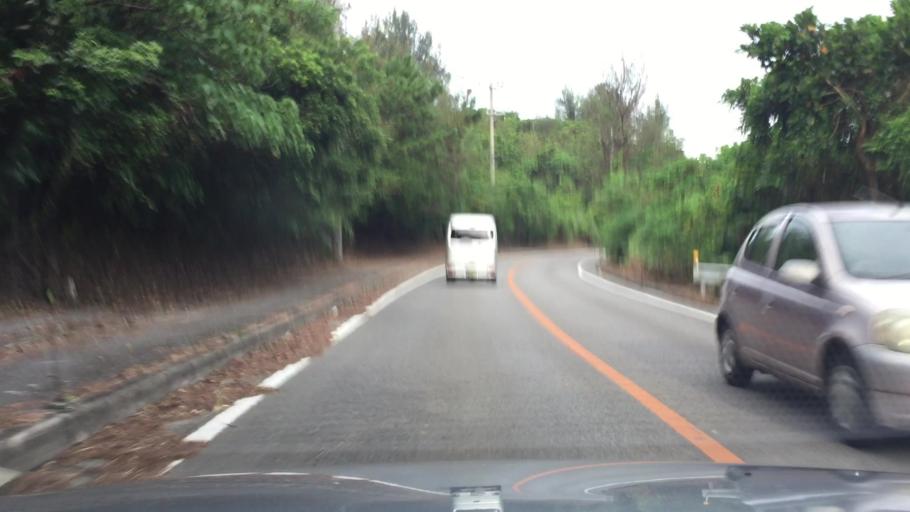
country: JP
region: Okinawa
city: Ishigaki
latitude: 24.4035
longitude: 124.1482
